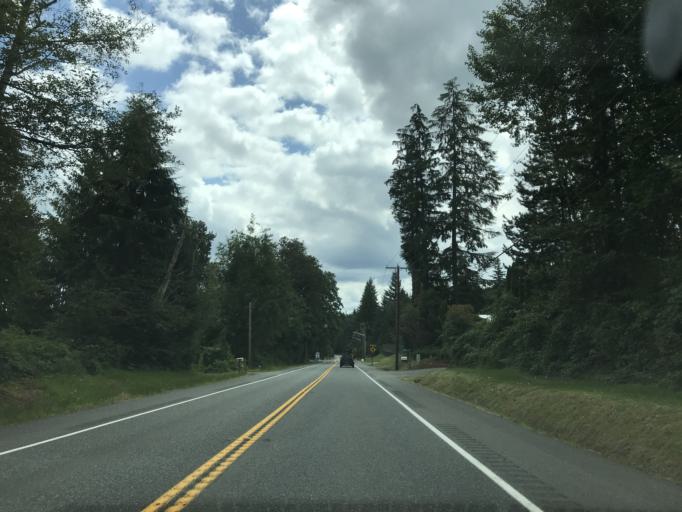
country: US
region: Washington
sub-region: King County
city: Maple Heights-Lake Desire
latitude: 47.4320
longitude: -122.1135
